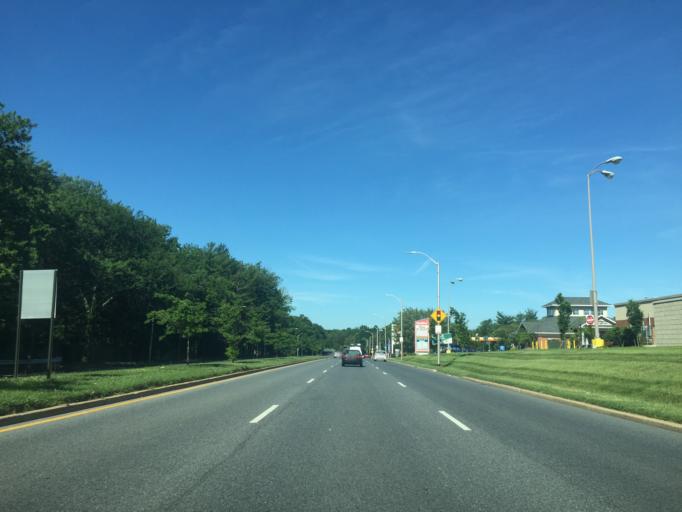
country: US
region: Maryland
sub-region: Baltimore County
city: Lochearn
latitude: 39.3452
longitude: -76.6989
